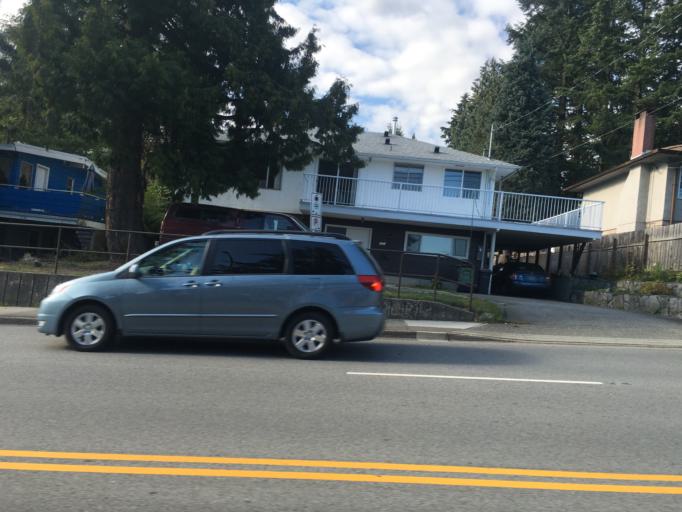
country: CA
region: British Columbia
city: Port Moody
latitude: 49.2490
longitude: -122.8503
